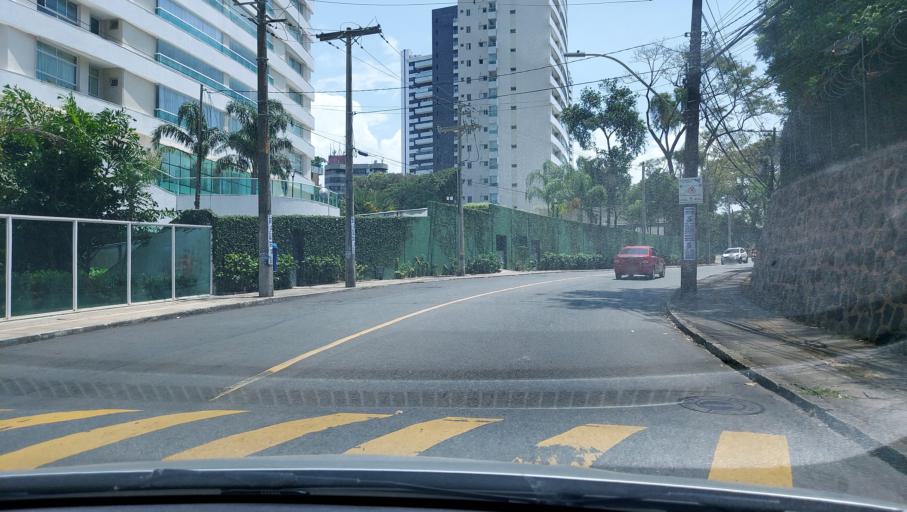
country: BR
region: Bahia
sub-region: Salvador
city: Salvador
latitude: -12.9981
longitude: -38.4869
